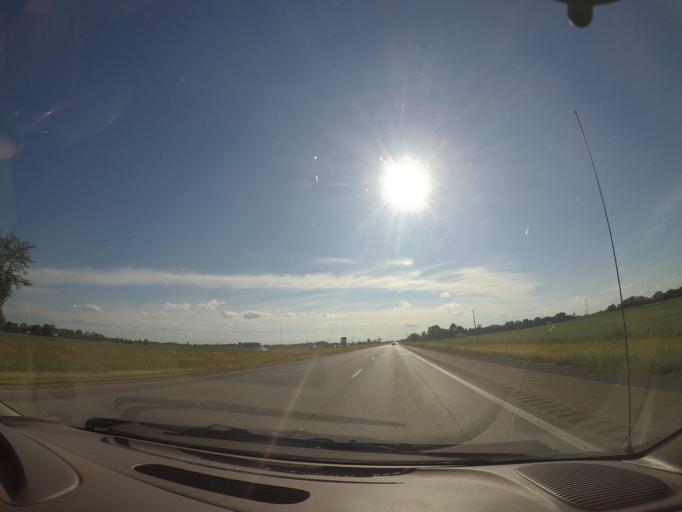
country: US
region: Ohio
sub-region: Henry County
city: Napoleon
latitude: 41.4172
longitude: -84.0711
